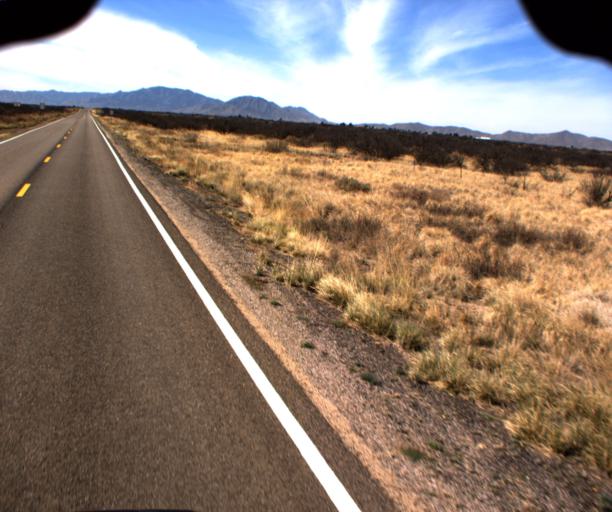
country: US
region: Arizona
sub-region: Cochise County
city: Willcox
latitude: 32.1236
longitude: -109.9094
